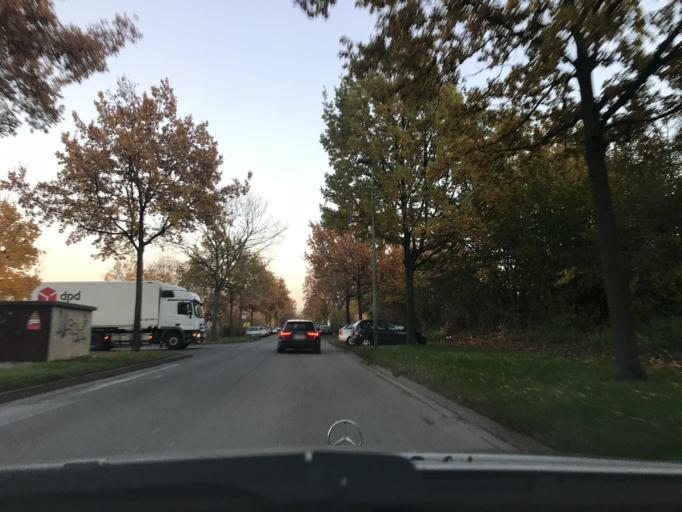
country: DE
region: North Rhine-Westphalia
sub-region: Regierungsbezirk Arnsberg
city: Bad Sassendorf
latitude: 51.5544
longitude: 8.1520
